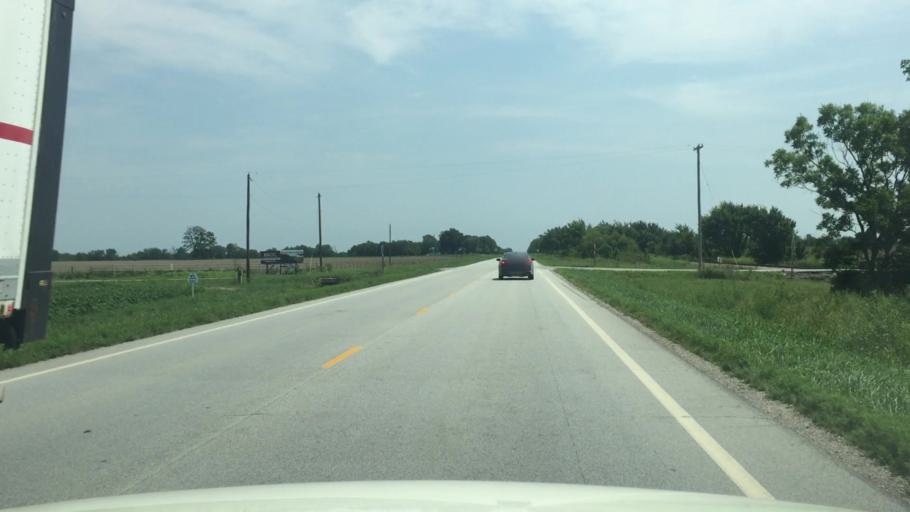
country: US
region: Kansas
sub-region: Cherokee County
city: Columbus
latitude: 37.1788
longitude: -94.8871
